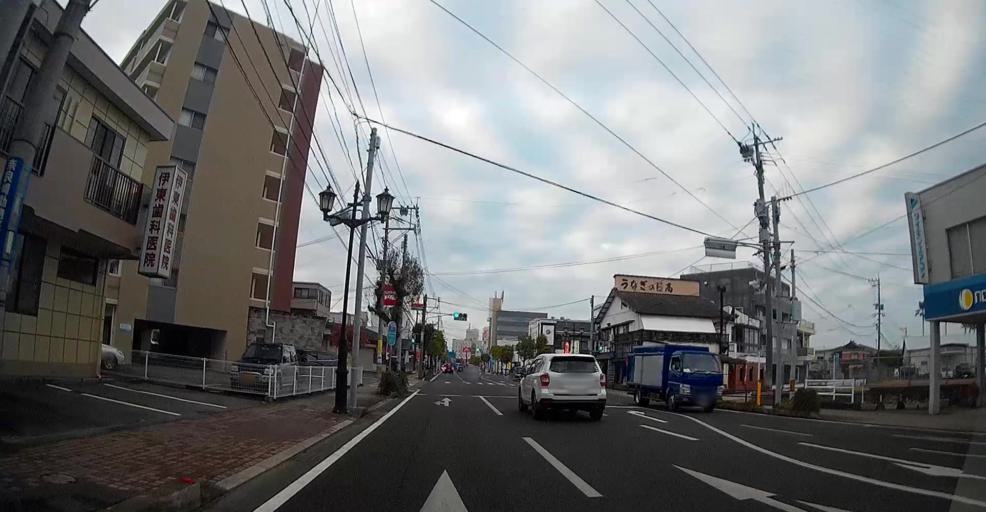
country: JP
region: Kumamoto
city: Hondo
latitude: 32.4523
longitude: 130.1961
